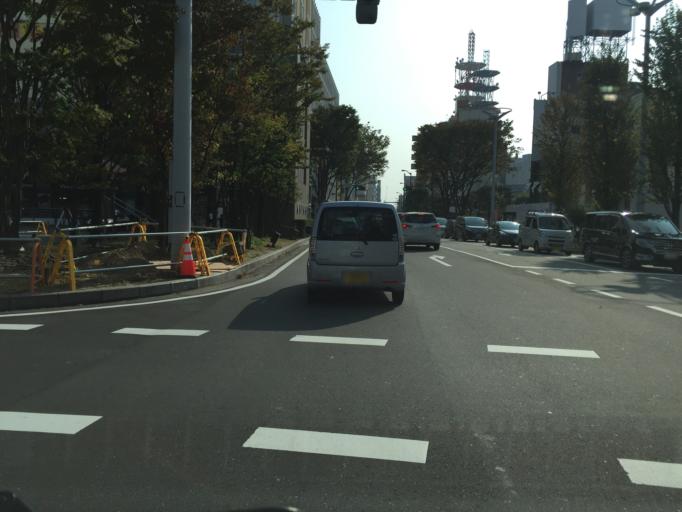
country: JP
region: Fukushima
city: Koriyama
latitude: 37.3978
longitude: 140.3873
